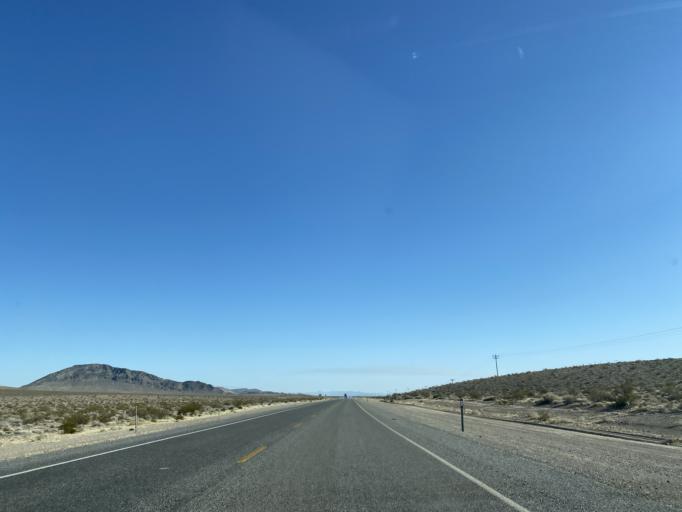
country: US
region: Nevada
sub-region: Nye County
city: Beatty
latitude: 36.7662
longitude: -116.6761
